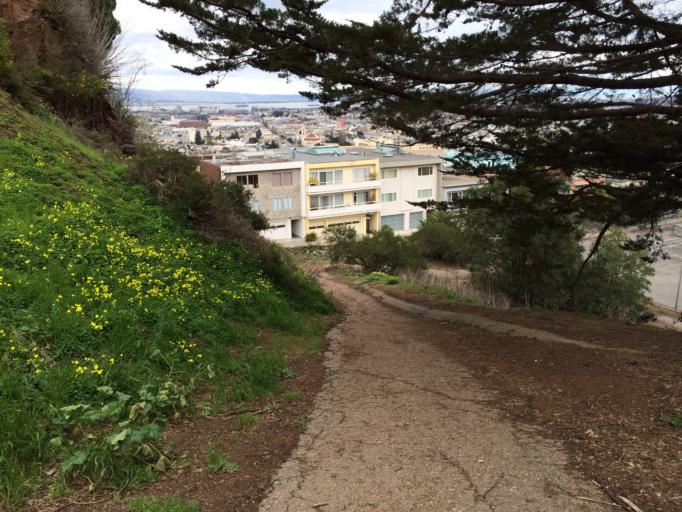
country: US
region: California
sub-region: San Francisco County
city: San Francisco
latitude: 37.7647
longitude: -122.4376
